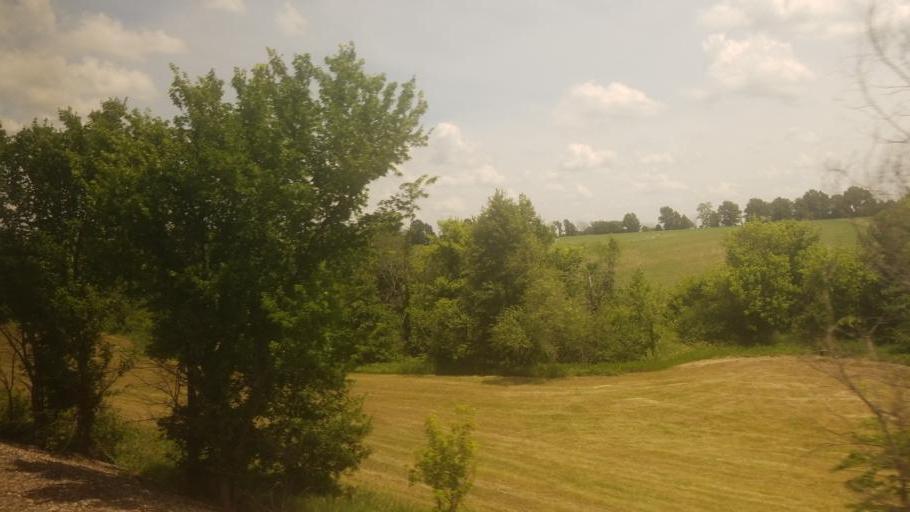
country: US
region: Missouri
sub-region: Macon County
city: La Plata
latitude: 40.0559
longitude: -92.4647
